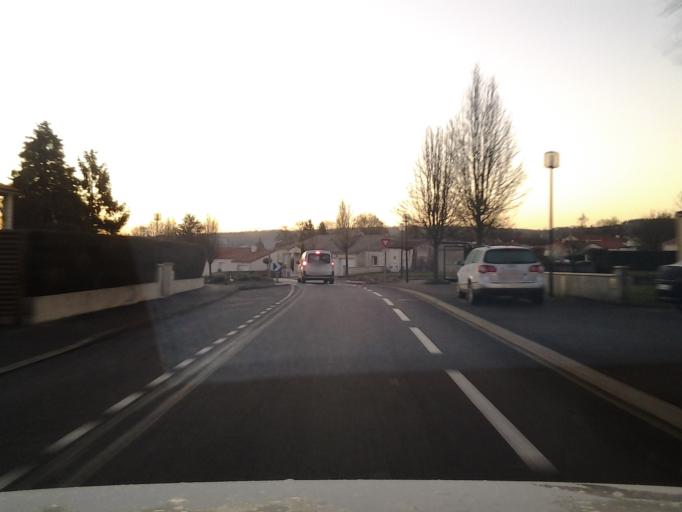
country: FR
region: Pays de la Loire
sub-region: Departement de la Vendee
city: Les Epesses
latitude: 46.8800
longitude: -0.9040
